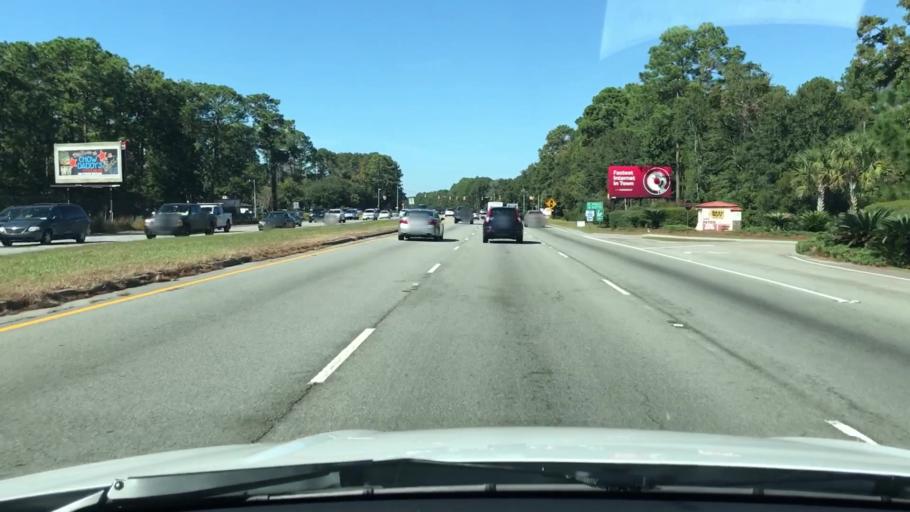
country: US
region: South Carolina
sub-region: Beaufort County
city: Bluffton
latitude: 32.2581
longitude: -80.8507
